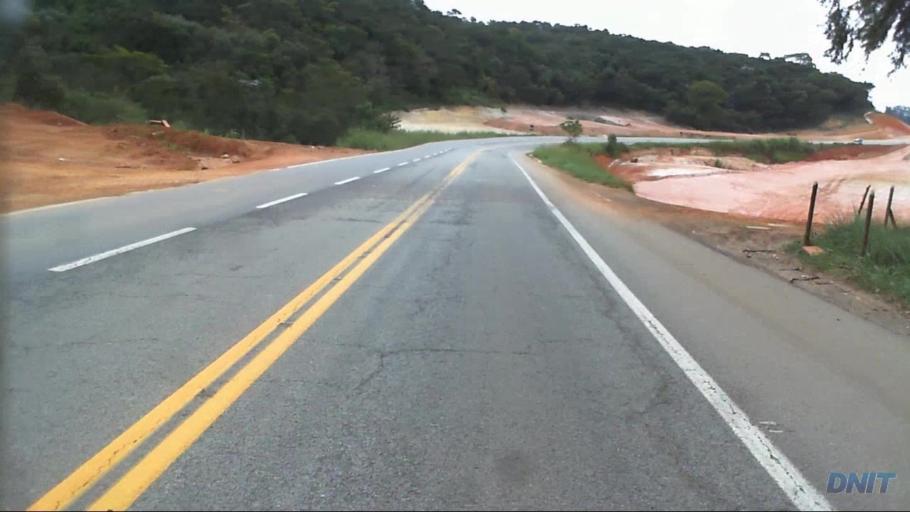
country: BR
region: Minas Gerais
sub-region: Caete
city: Caete
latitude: -19.7472
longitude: -43.5461
